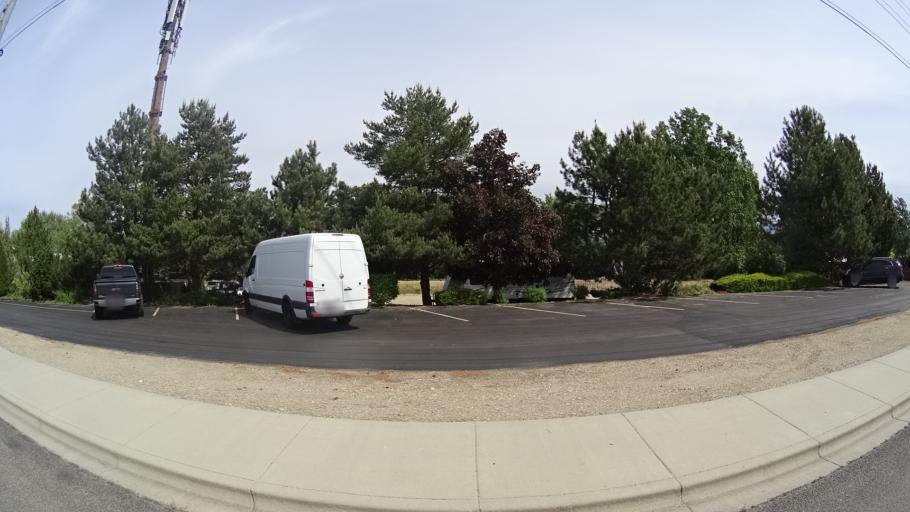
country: US
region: Idaho
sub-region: Ada County
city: Garden City
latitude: 43.5757
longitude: -116.3119
